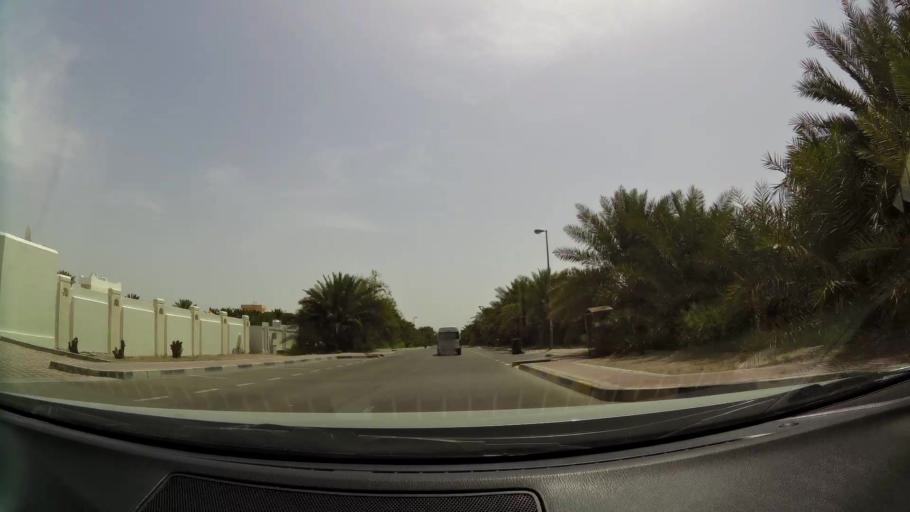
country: AE
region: Abu Dhabi
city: Al Ain
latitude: 24.1744
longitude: 55.7098
